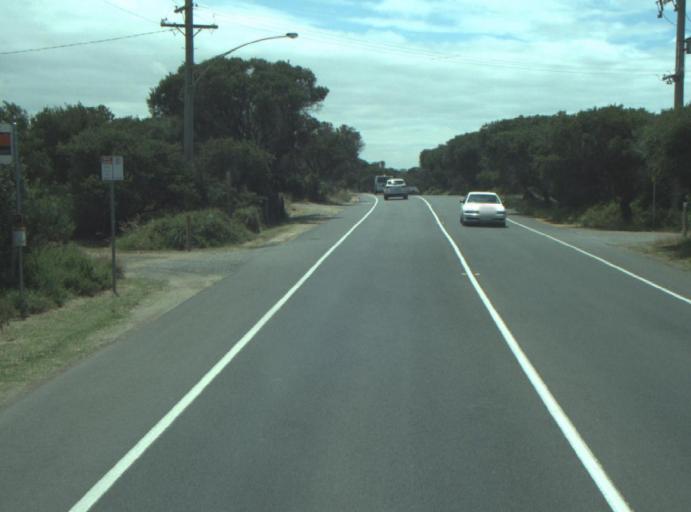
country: AU
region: Victoria
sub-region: Greater Geelong
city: Leopold
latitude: -38.2765
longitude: 144.5030
